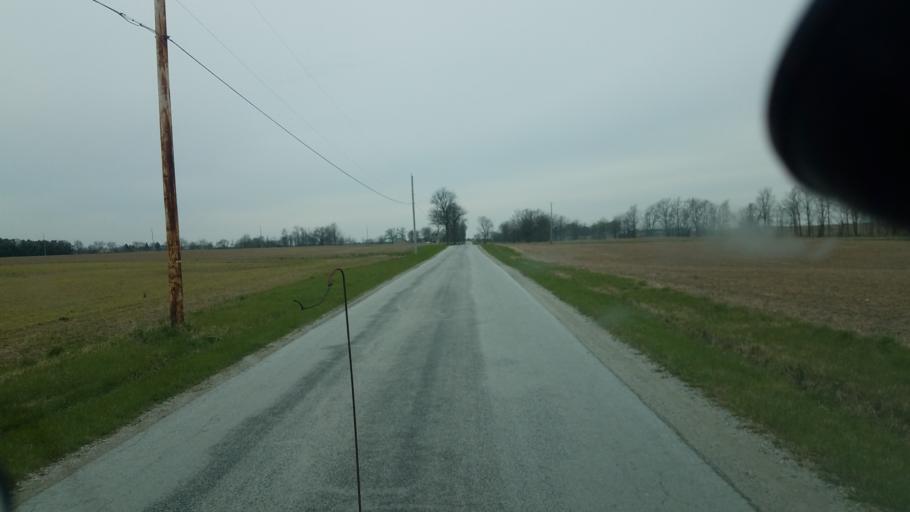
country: US
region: Ohio
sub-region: Hardin County
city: Forest
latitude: 40.8179
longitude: -83.4901
